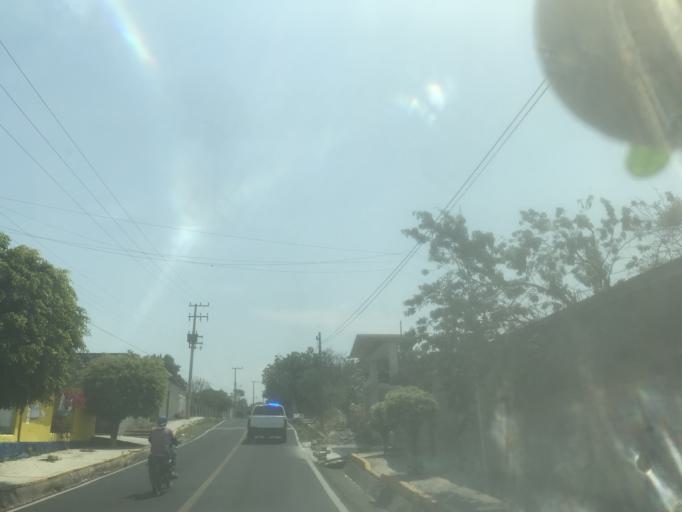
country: MX
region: Mexico
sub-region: Atlautla
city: San Andres Tlalamac
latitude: 18.9662
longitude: -98.8197
